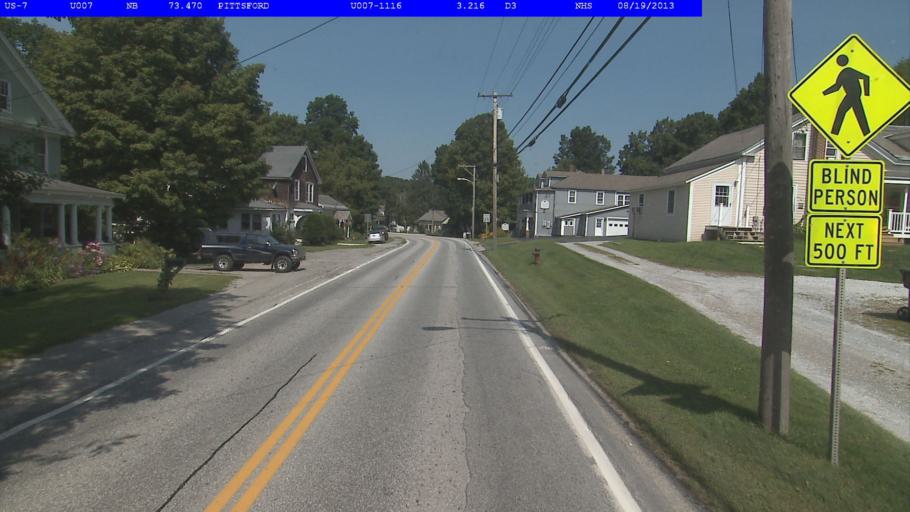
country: US
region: Vermont
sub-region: Rutland County
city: Rutland
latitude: 43.7052
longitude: -73.0139
